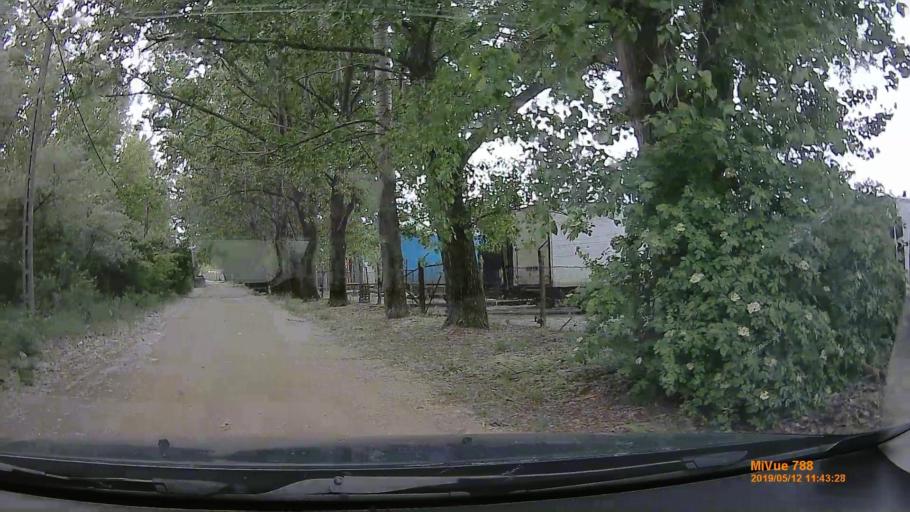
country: HU
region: Budapest
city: Budapest XVII. keruelet
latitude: 47.4629
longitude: 19.2539
